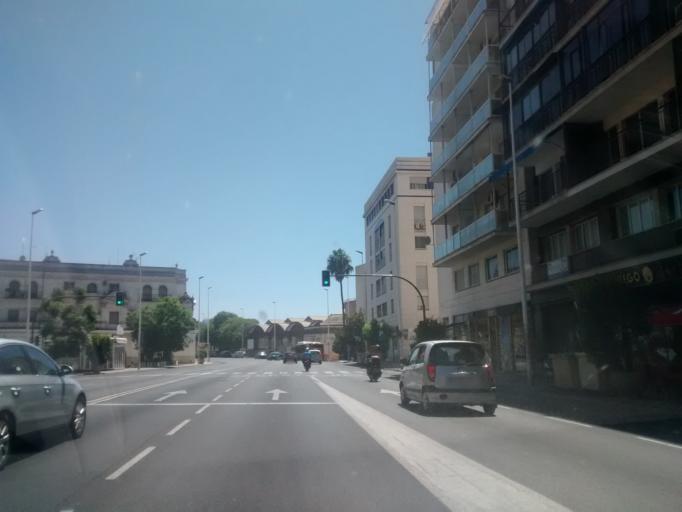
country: ES
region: Andalusia
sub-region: Provincia de Sevilla
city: Sevilla
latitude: 37.3891
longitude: -6.0024
